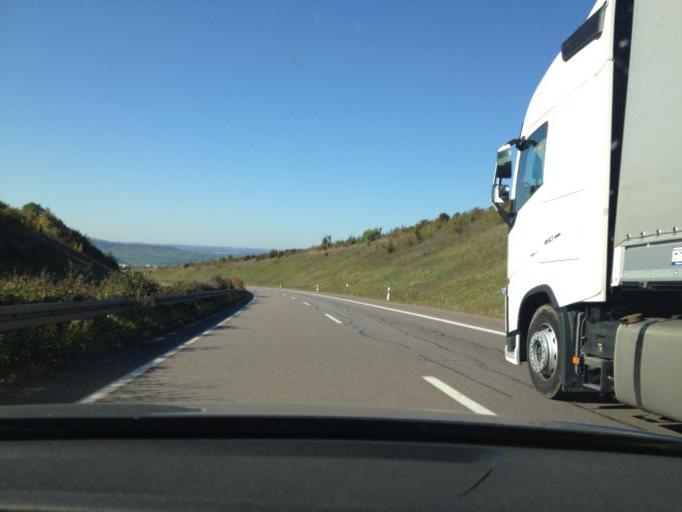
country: DE
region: Saarland
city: Perl
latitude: 49.4920
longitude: 6.4074
